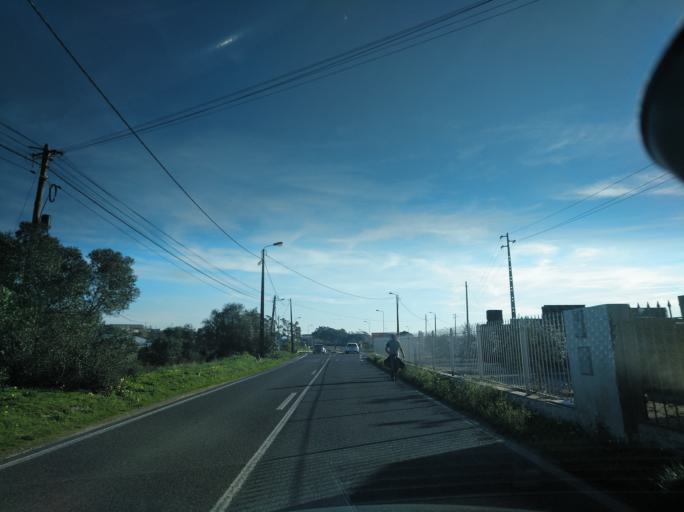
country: PT
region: Lisbon
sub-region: Sintra
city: Pero Pinheiro
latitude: 38.8746
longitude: -9.3298
